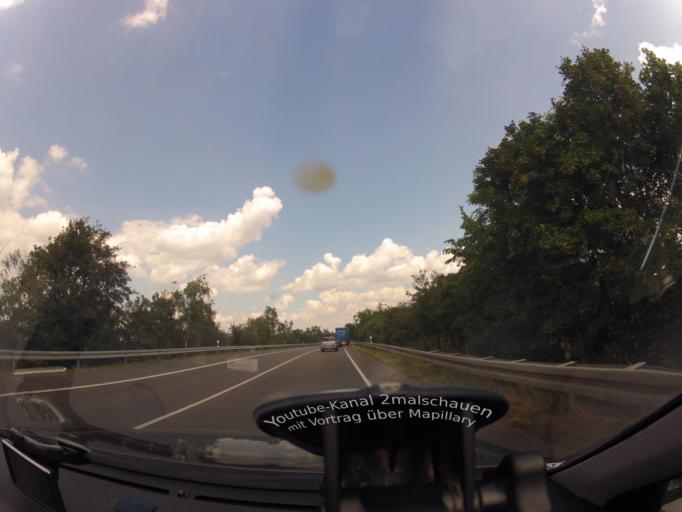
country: DE
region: Saxony
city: Doberschutz
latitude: 51.4864
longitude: 12.7291
